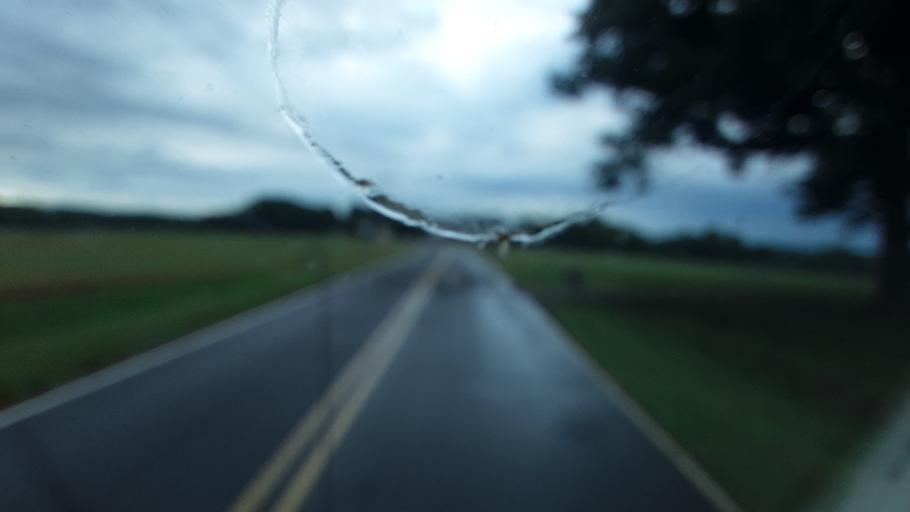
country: US
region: North Carolina
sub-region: Yadkin County
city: Jonesville
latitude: 36.0539
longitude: -80.8316
